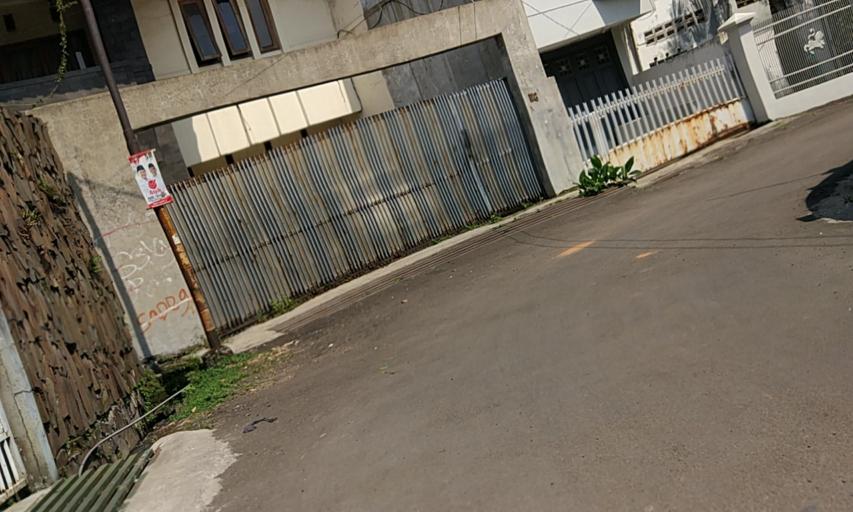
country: ID
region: West Java
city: Margahayukencana
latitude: -6.9211
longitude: 107.5575
